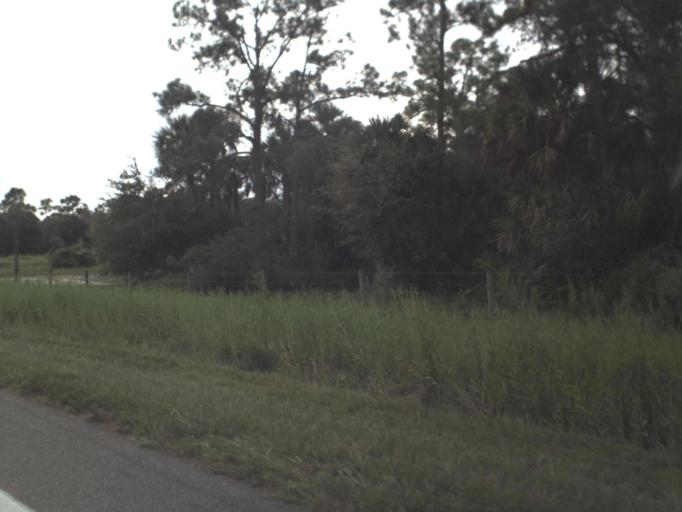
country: US
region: Florida
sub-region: Charlotte County
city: Cleveland
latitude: 26.9595
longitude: -81.7608
